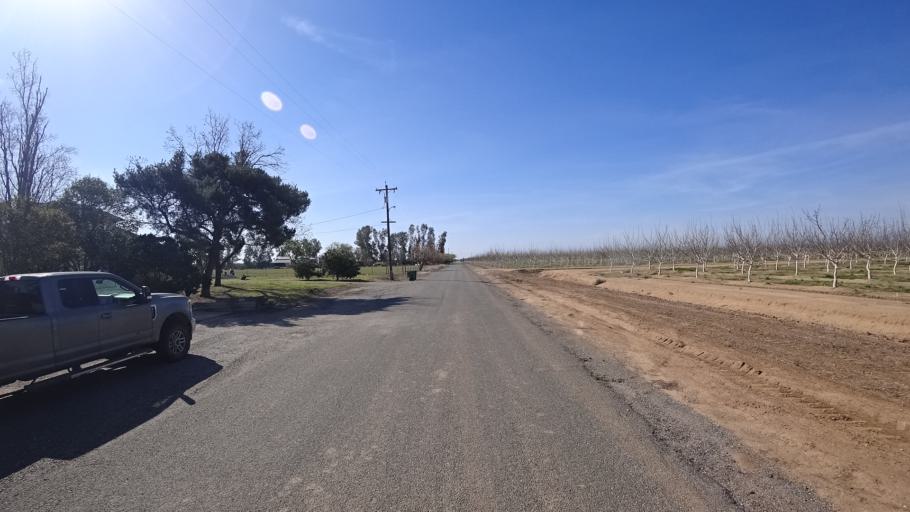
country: US
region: California
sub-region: Glenn County
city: Willows
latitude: 39.6183
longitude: -122.2129
